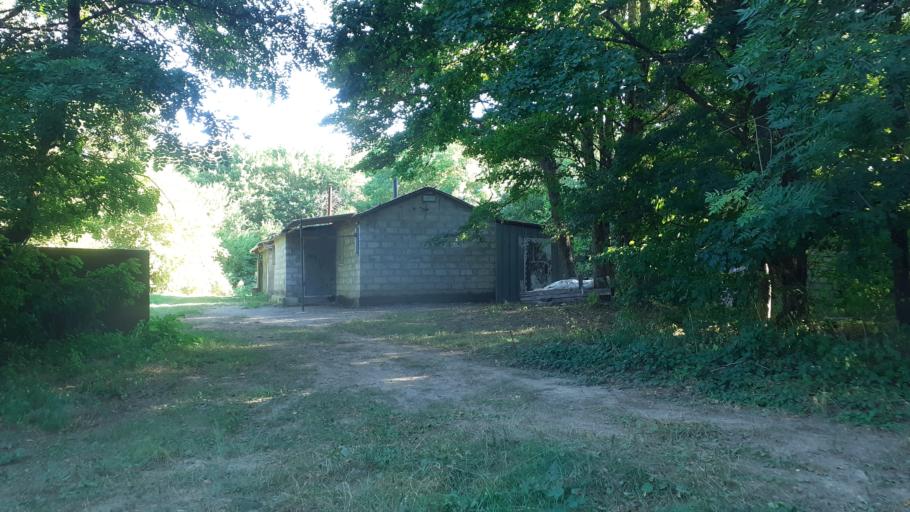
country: RU
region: Krasnodarskiy
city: Chernomorskiy
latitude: 44.6615
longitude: 38.4847
